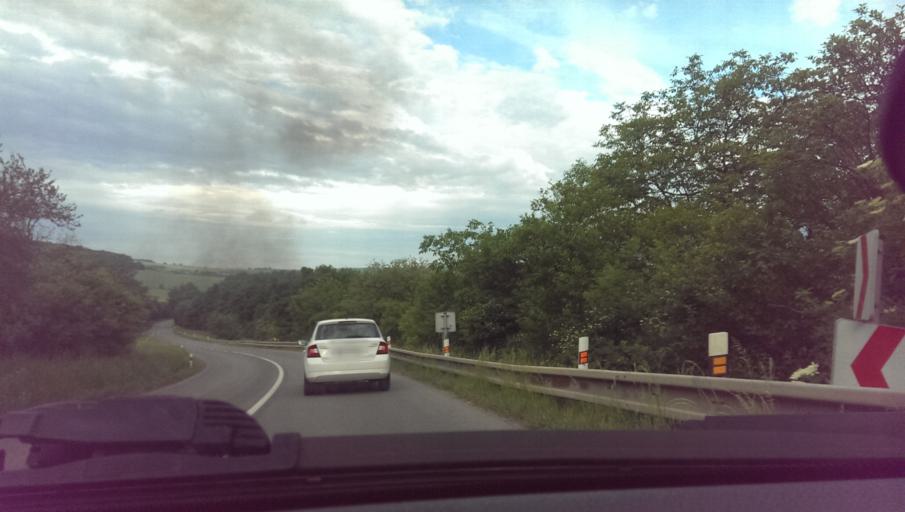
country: CZ
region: Zlin
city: Kvasice
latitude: 49.2486
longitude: 17.4596
